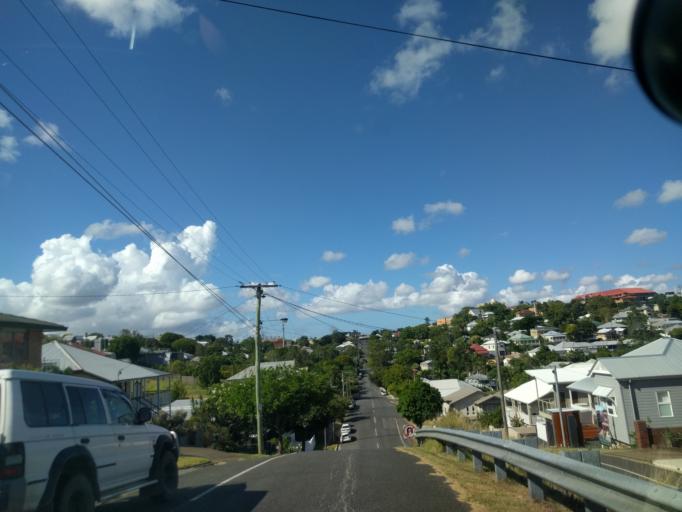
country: AU
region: Queensland
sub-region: Brisbane
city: Milton
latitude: -27.4582
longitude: 153.0030
